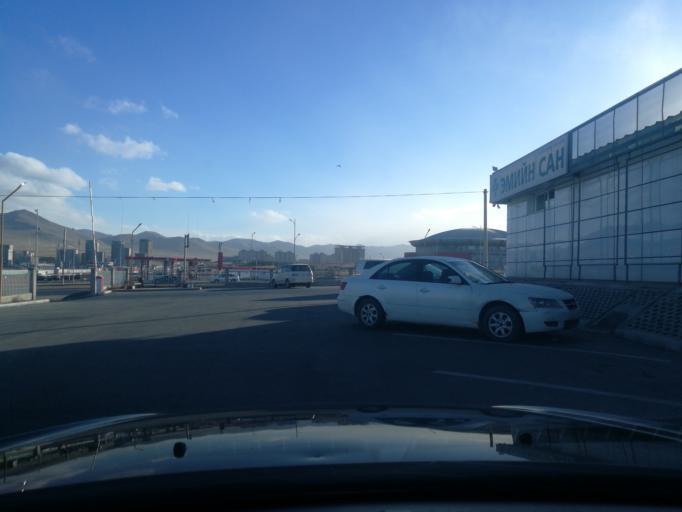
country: MN
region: Ulaanbaatar
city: Ulaanbaatar
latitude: 47.8584
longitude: 106.7856
